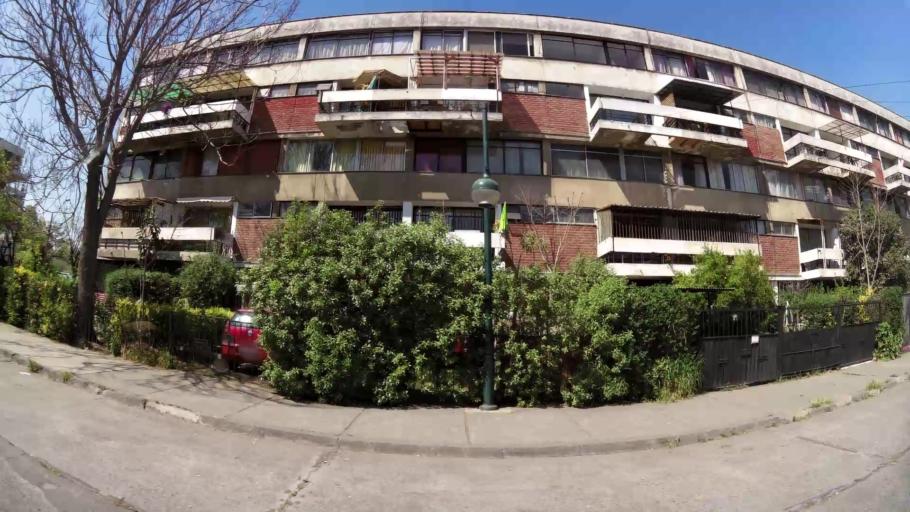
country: CL
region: Santiago Metropolitan
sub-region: Provincia de Santiago
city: Villa Presidente Frei, Nunoa, Santiago, Chile
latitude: -33.4611
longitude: -70.5847
